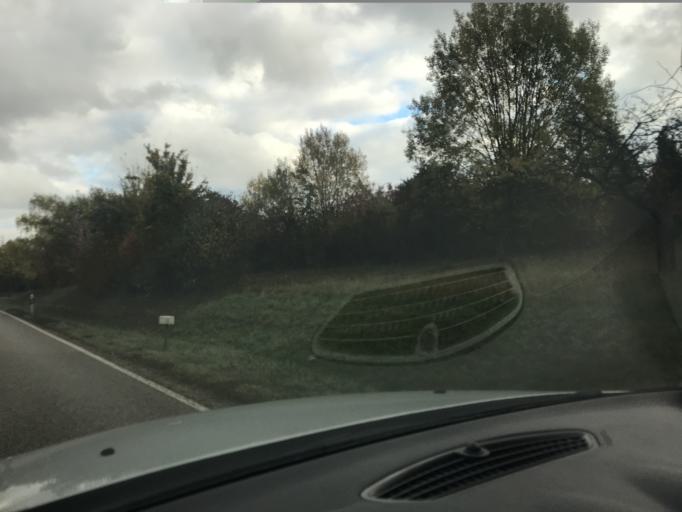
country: DE
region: Baden-Wuerttemberg
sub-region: Regierungsbezirk Stuttgart
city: Grossbottwar
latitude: 49.0051
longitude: 9.2632
